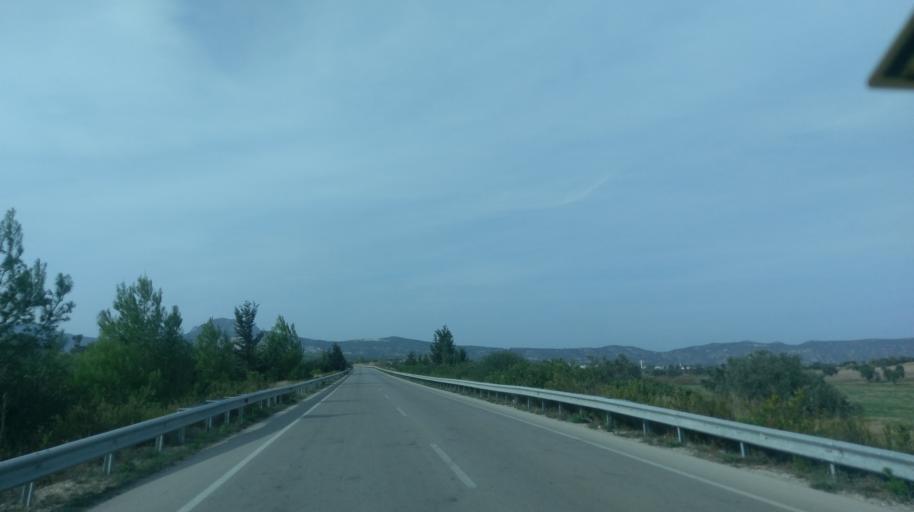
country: CY
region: Ammochostos
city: Leonarisso
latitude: 35.3958
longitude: 34.0033
